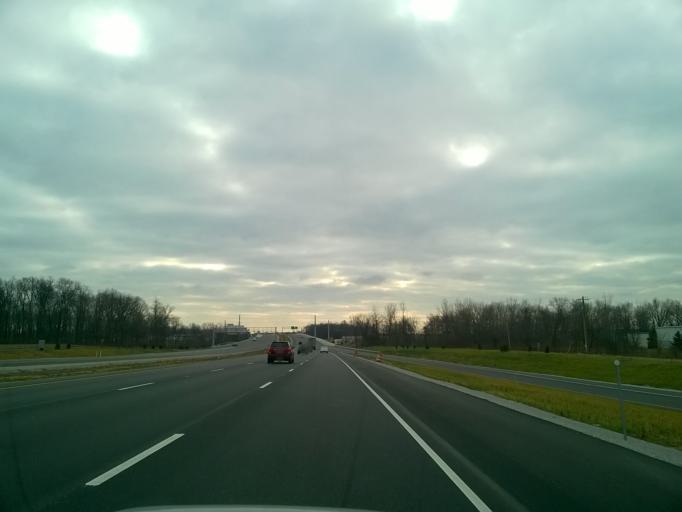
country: US
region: Indiana
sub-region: Hamilton County
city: Westfield
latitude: 40.0359
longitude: -86.1360
